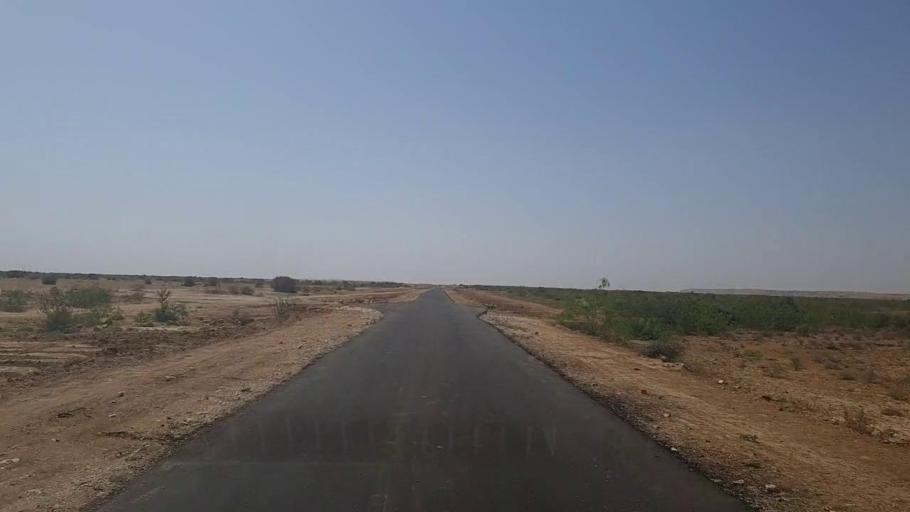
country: PK
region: Sindh
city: Kotri
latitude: 25.1498
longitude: 68.2173
